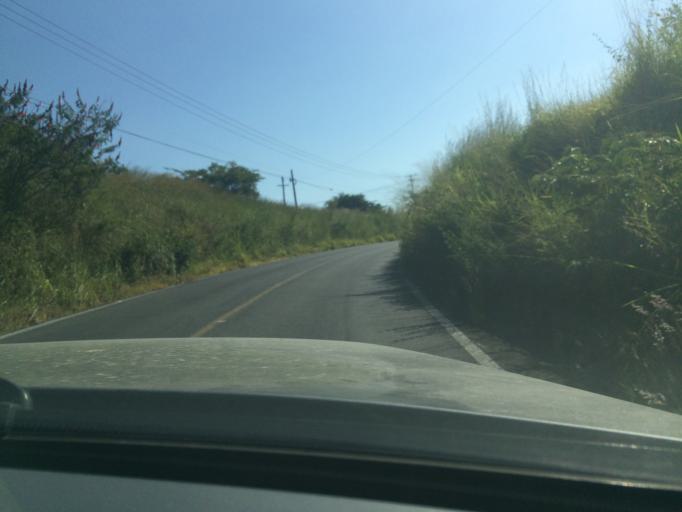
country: MX
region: Colima
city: Suchitlan
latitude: 19.3553
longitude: -103.7297
